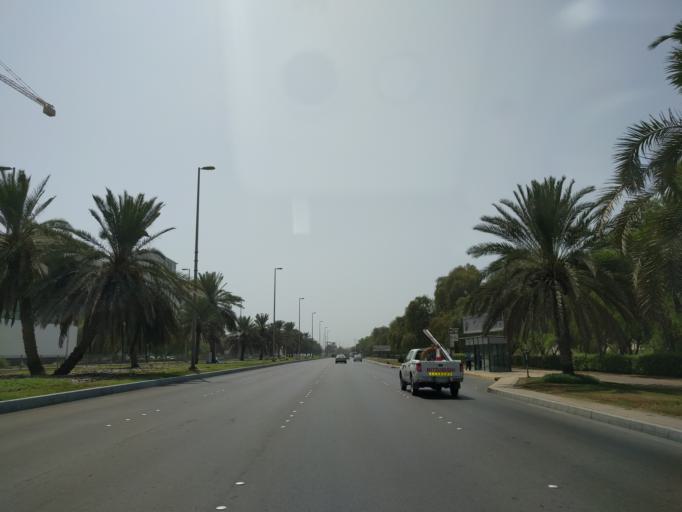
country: AE
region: Abu Dhabi
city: Abu Dhabi
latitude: 24.4399
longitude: 54.4113
